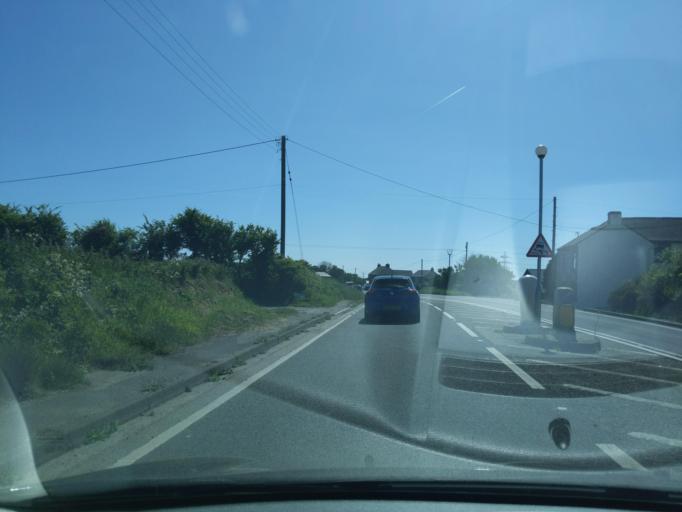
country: GB
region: England
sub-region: Cornwall
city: Wendron
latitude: 50.1614
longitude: -5.1841
